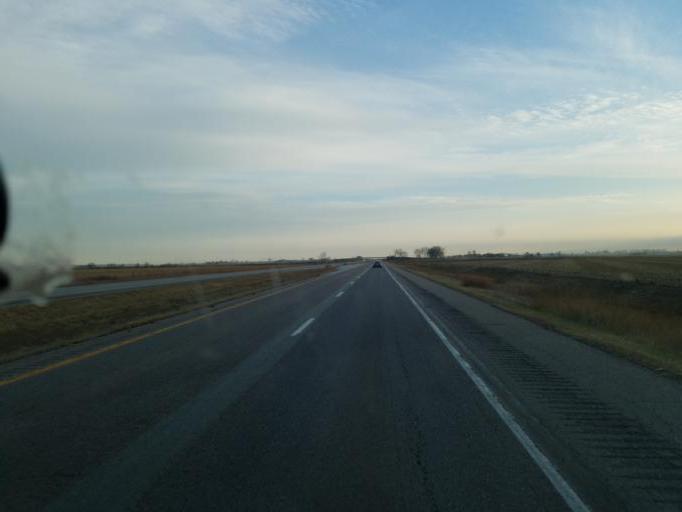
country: US
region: Nebraska
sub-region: Washington County
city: Blair
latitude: 41.6778
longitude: -96.0394
